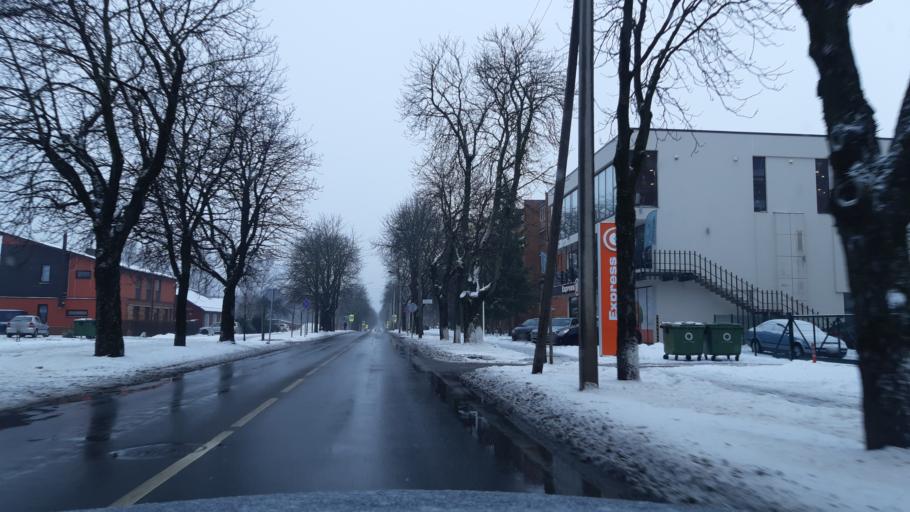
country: LT
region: Kauno apskritis
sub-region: Kaunas
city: Eiguliai
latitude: 54.9107
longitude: 23.9421
